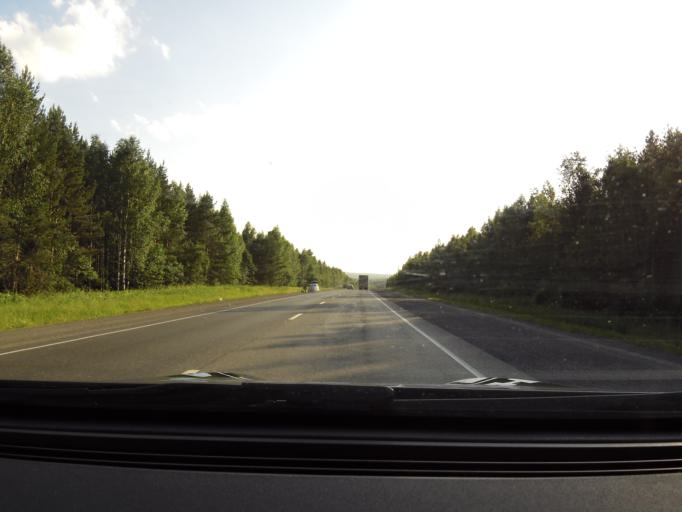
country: RU
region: Sverdlovsk
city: Druzhinino
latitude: 56.8425
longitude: 59.6713
